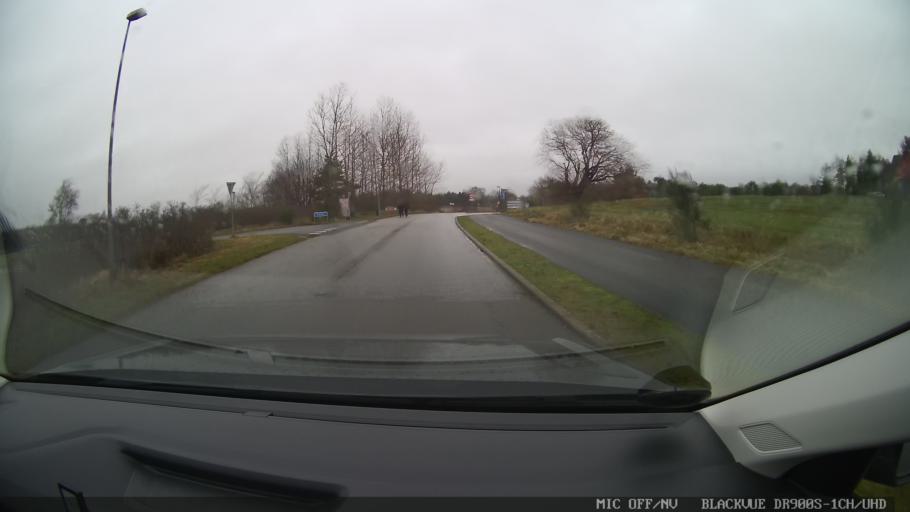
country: DK
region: Central Jutland
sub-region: Viborg Kommune
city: Karup
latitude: 56.2944
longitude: 9.1444
